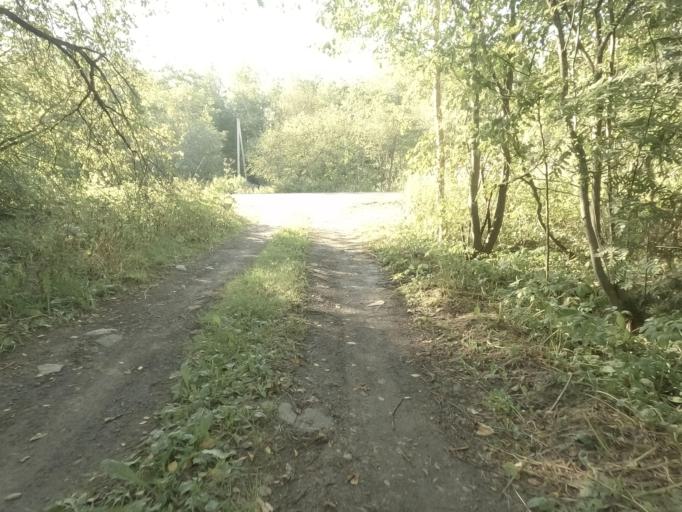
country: RU
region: Leningrad
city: Kirovsk
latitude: 59.9253
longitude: 30.9745
